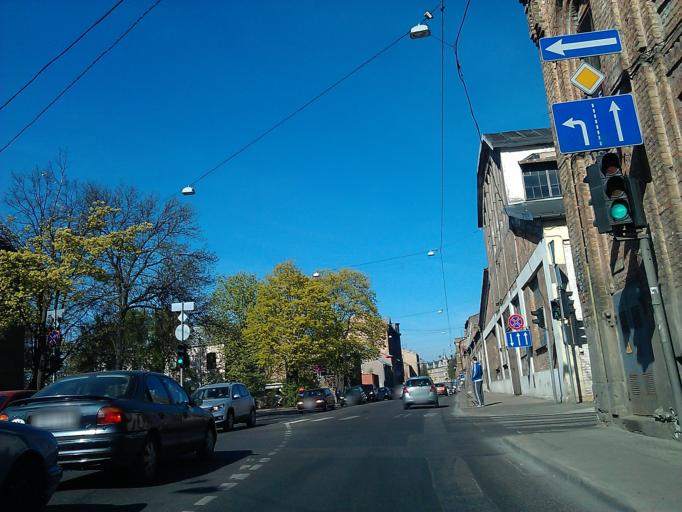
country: LV
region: Riga
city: Riga
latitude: 56.9489
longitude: 24.1456
